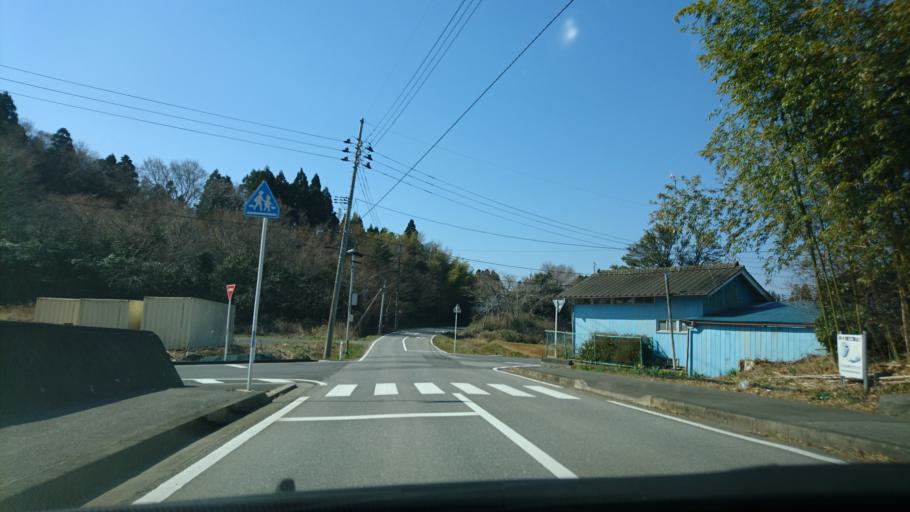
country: JP
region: Iwate
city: Ofunato
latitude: 38.8626
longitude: 141.6096
